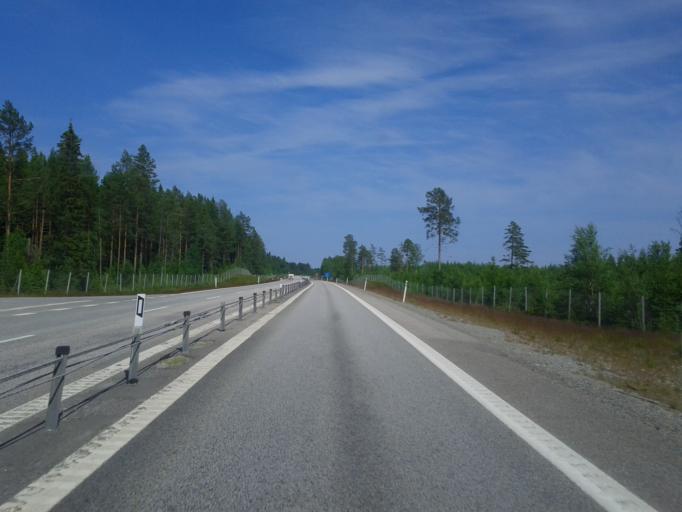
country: SE
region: Vaesterbotten
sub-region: Umea Kommun
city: Hoernefors
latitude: 63.6327
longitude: 19.8889
